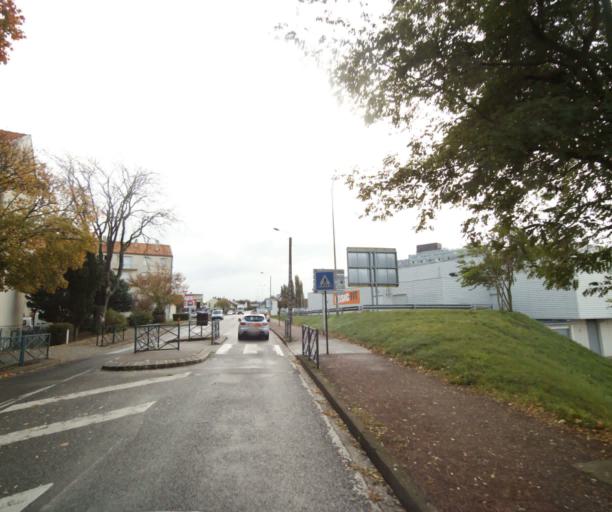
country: FR
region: Centre
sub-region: Departement d'Eure-et-Loir
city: Vernouillet
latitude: 48.7298
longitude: 1.3815
